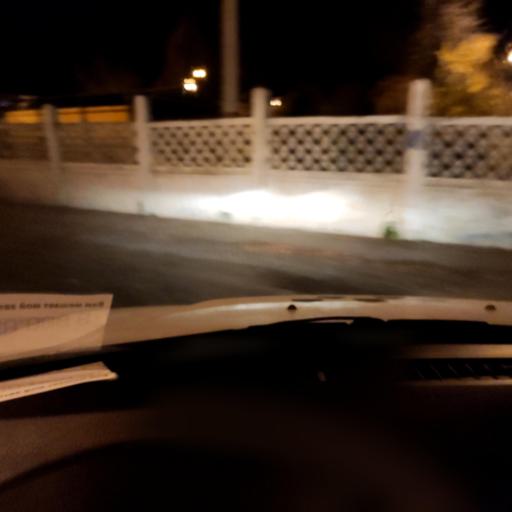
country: RU
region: Samara
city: Tol'yatti
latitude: 53.5066
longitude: 49.3953
